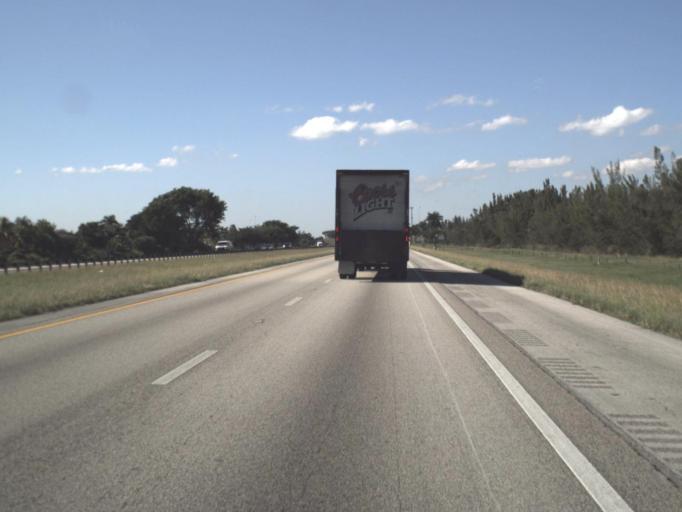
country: US
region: Florida
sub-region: Miami-Dade County
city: Palm Springs North
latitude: 25.9557
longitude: -80.3432
